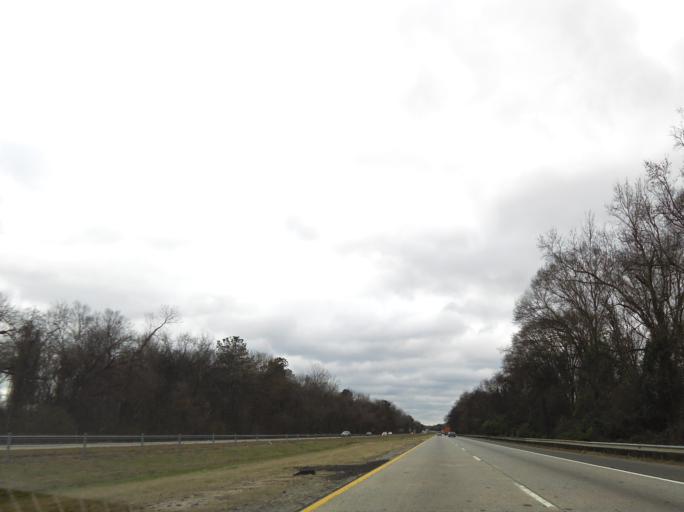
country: US
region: Georgia
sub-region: Bibb County
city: Macon
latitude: 32.8352
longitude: -83.6118
